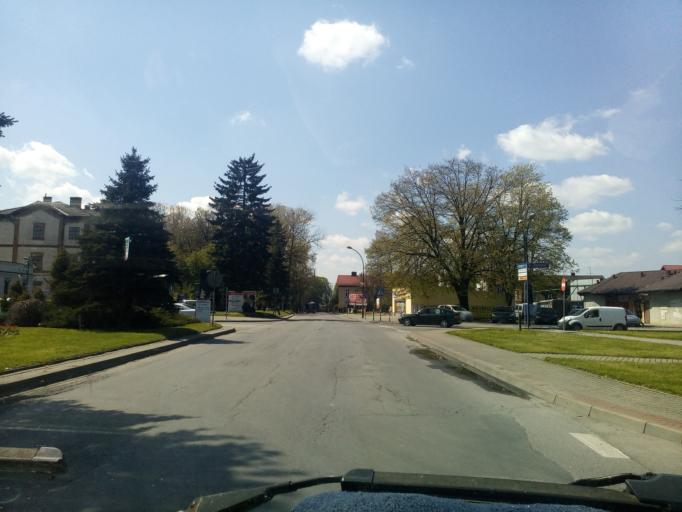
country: PL
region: Lesser Poland Voivodeship
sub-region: Powiat nowosadecki
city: Nowy Sacz
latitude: 49.6073
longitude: 20.7030
